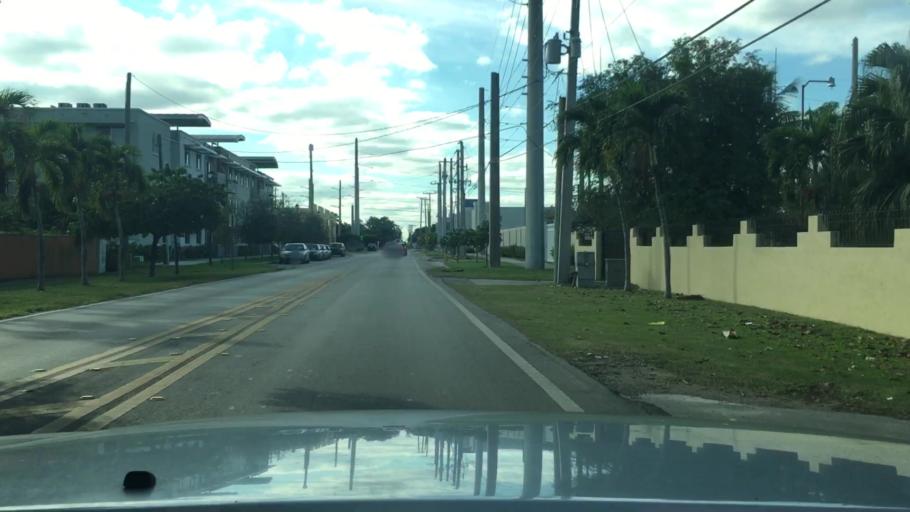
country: US
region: Florida
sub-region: Miami-Dade County
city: Princeton
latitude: 25.5366
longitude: -80.4022
